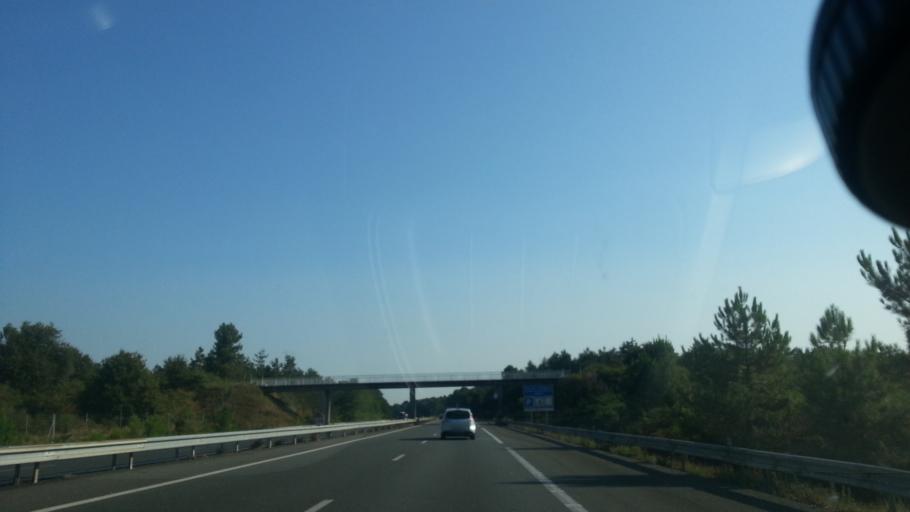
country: FR
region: Poitou-Charentes
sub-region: Departement de la Vienne
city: Chatellerault
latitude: 46.7873
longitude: 0.5063
